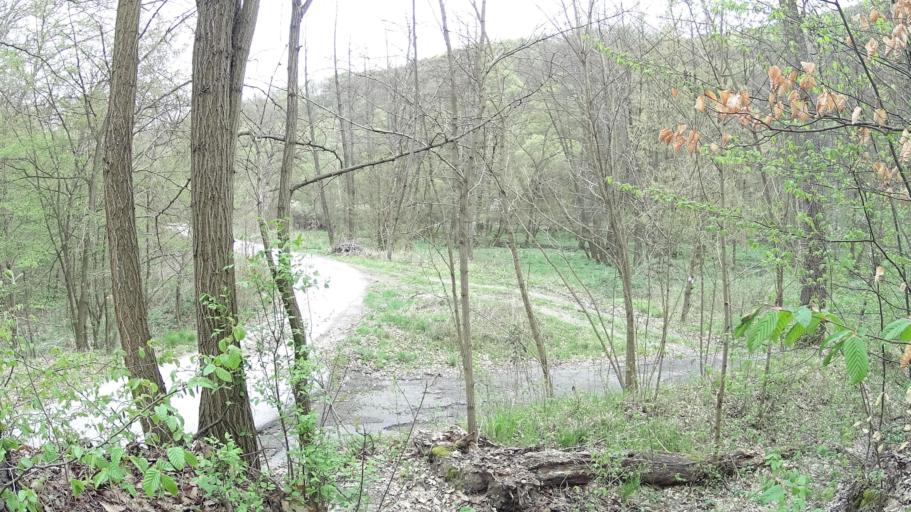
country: HU
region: Nograd
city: Diosjeno
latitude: 47.8863
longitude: 19.0432
